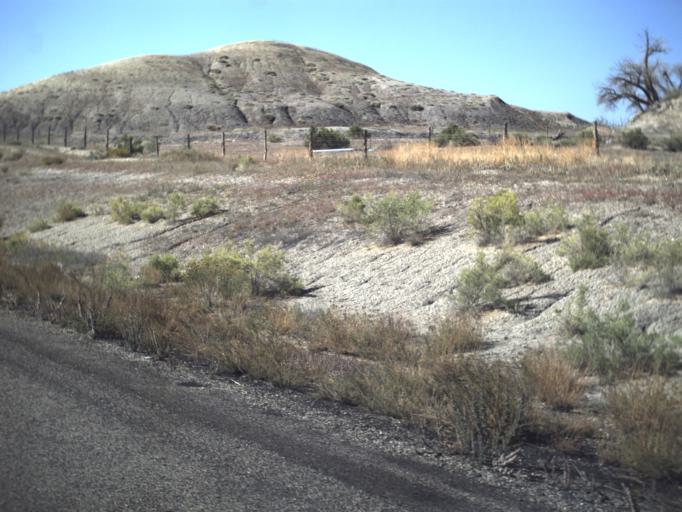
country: US
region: Utah
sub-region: Emery County
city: Castle Dale
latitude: 39.1776
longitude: -111.0494
